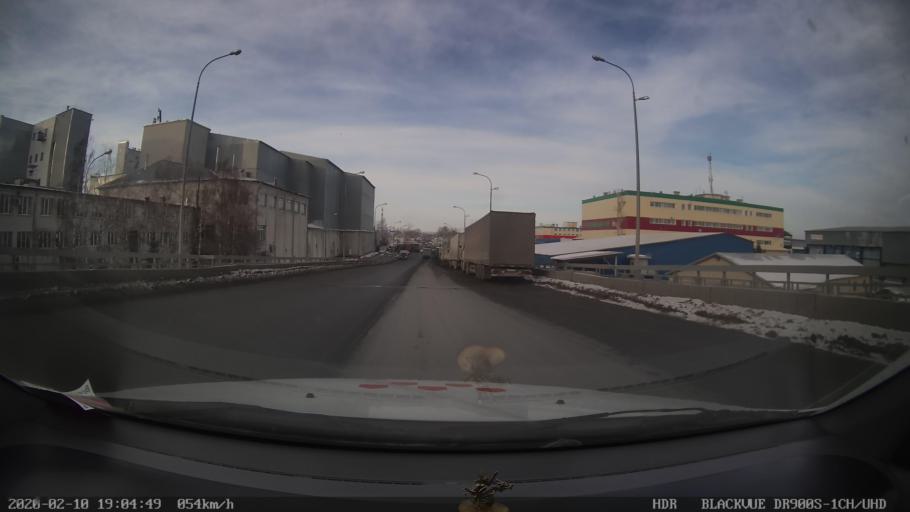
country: RU
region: Tatarstan
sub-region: Gorod Kazan'
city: Kazan
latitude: 55.7317
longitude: 49.1276
